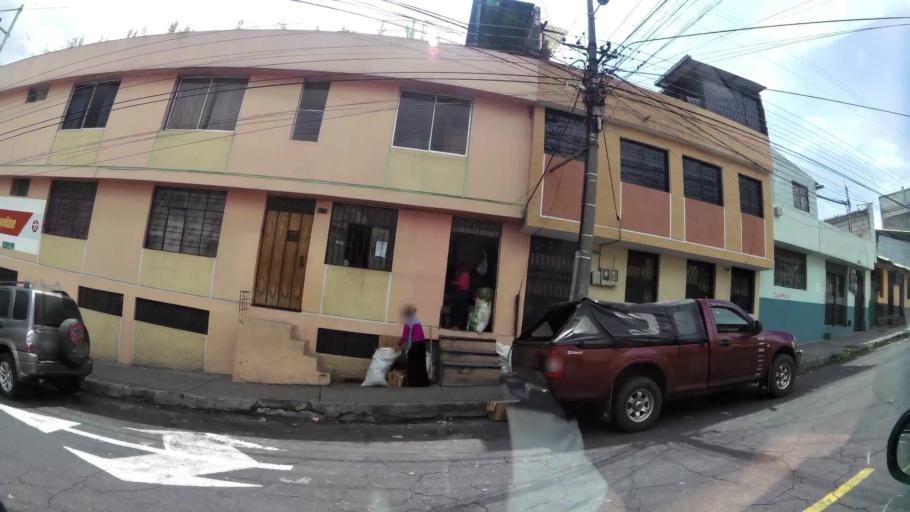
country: EC
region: Pichincha
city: Quito
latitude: -0.2576
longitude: -78.5175
